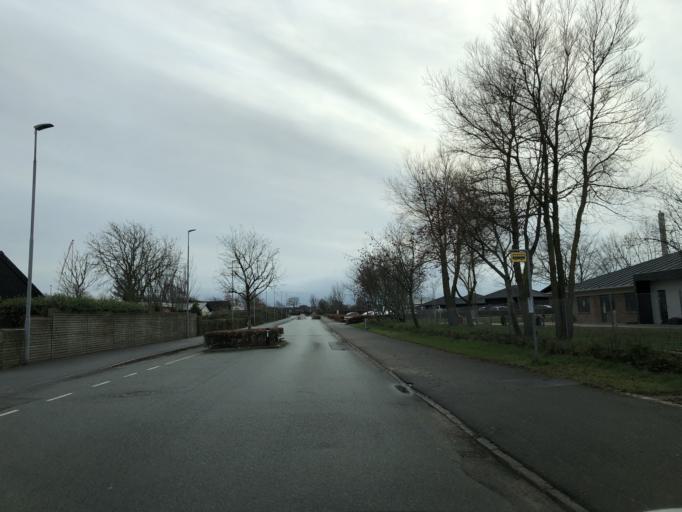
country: DK
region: Central Jutland
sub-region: Struer Kommune
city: Struer
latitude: 56.4863
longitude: 8.5746
